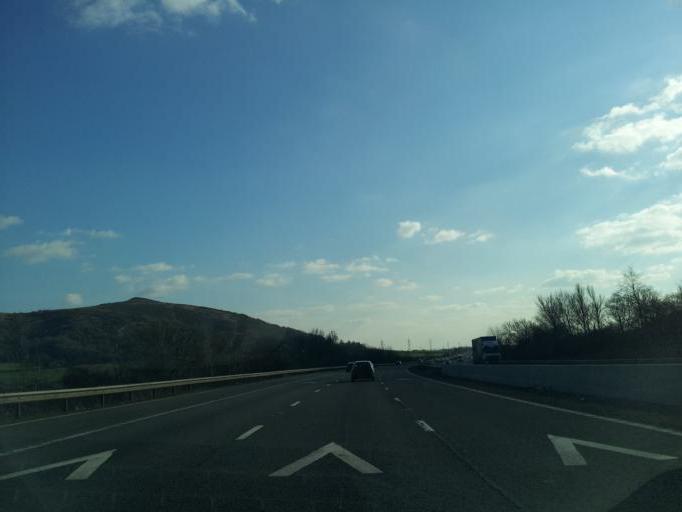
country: GB
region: England
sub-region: North Somerset
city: Banwell
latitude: 51.3122
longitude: -2.8850
